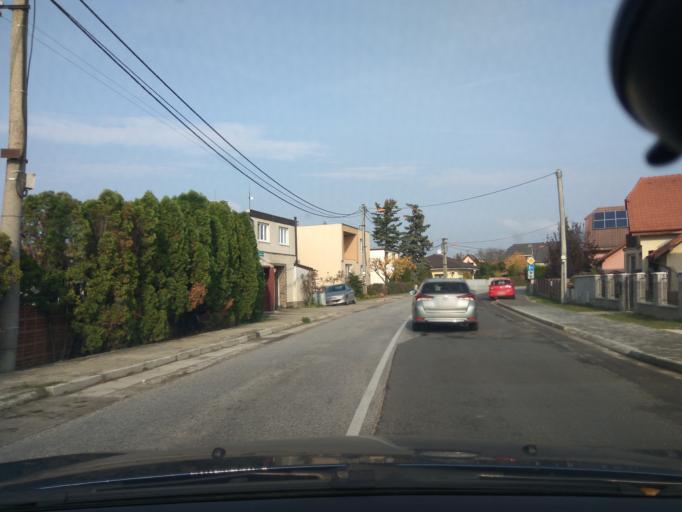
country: SK
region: Trnavsky
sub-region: Okres Trnava
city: Piestany
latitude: 48.6164
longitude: 17.7926
